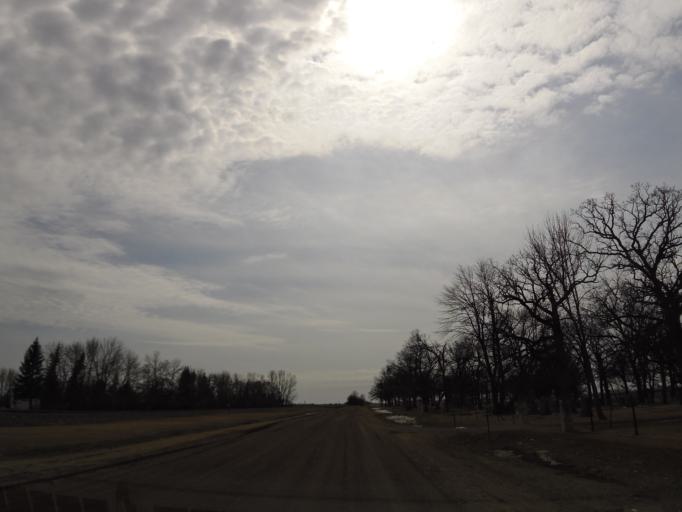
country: US
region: North Dakota
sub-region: Walsh County
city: Grafton
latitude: 48.2840
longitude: -97.3672
